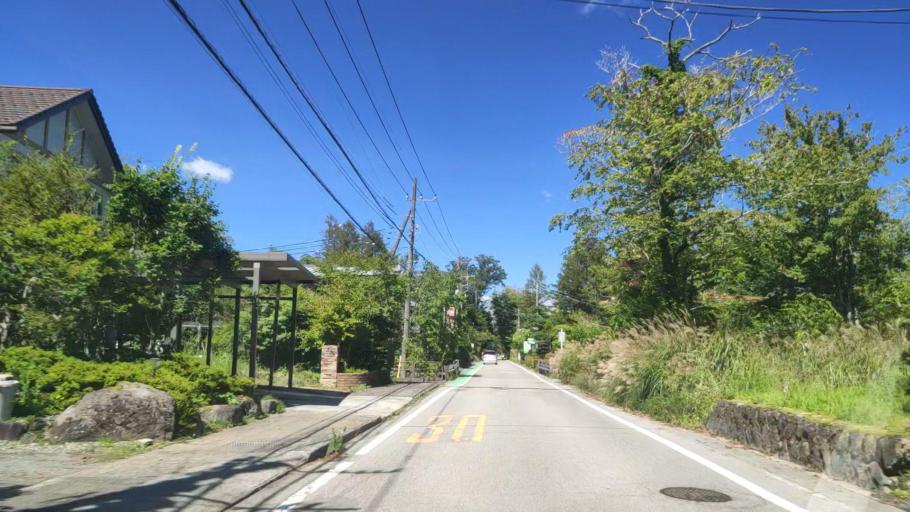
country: JP
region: Shizuoka
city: Gotemba
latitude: 35.4096
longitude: 138.8562
